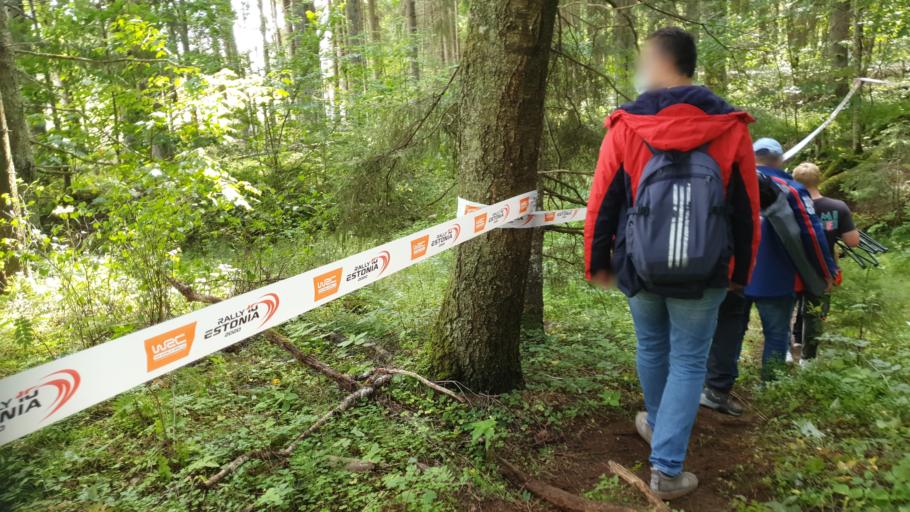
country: EE
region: Tartu
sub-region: UElenurme vald
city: Ulenurme
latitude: 58.1326
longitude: 26.7740
